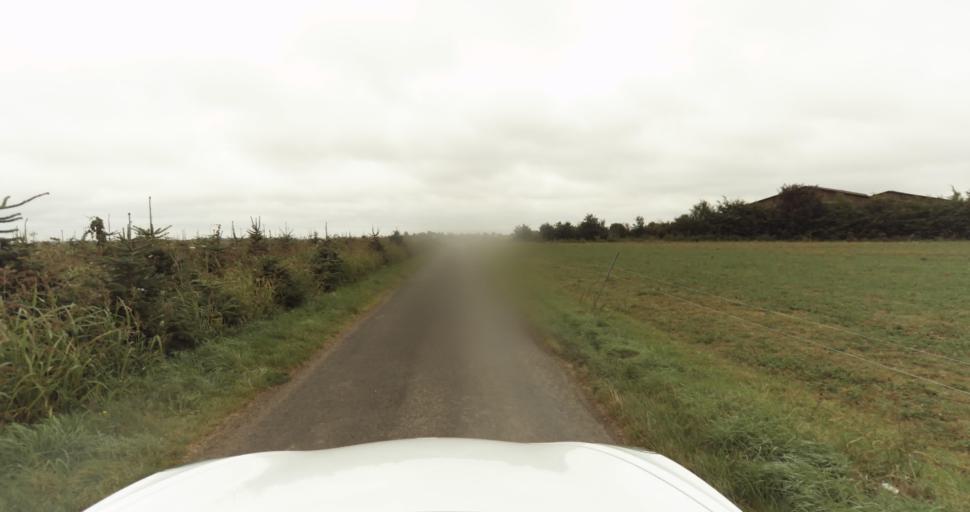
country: FR
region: Haute-Normandie
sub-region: Departement de l'Eure
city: Aviron
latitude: 49.0786
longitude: 1.0717
